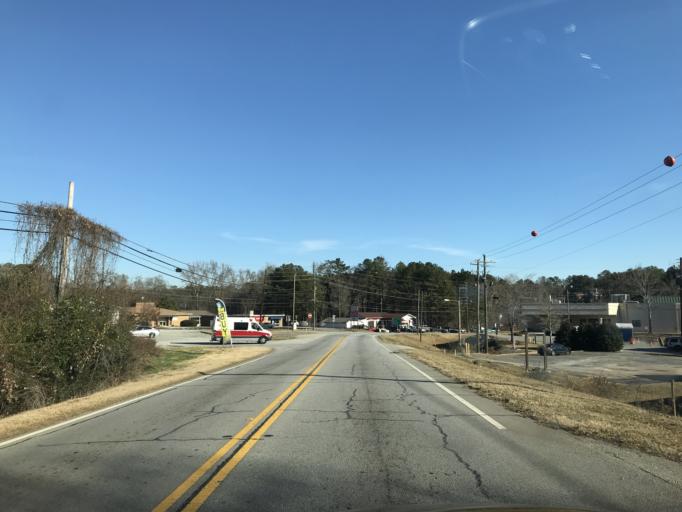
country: US
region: Georgia
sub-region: Paulding County
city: Dallas
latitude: 33.9193
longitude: -84.8541
